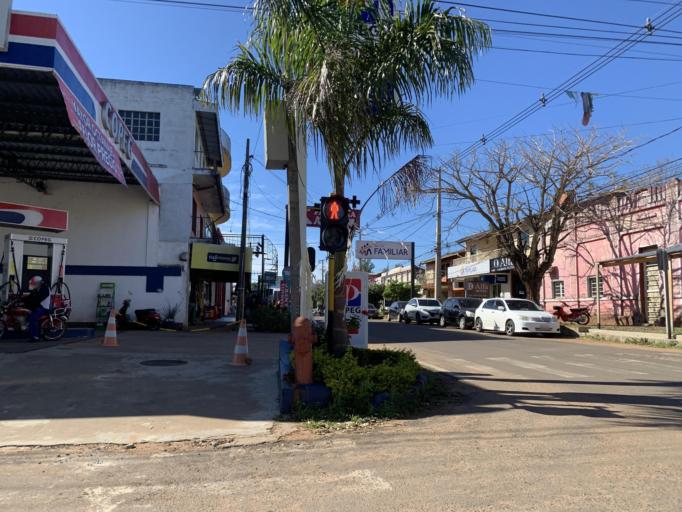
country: PY
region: Misiones
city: San Juan Bautista
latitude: -26.6688
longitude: -57.1416
